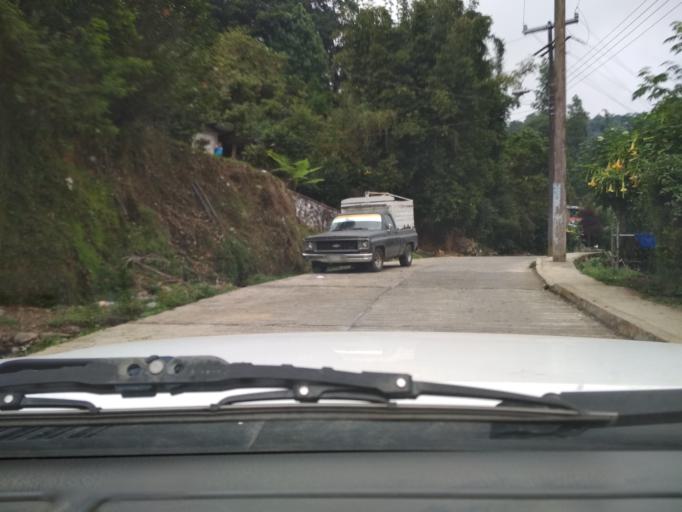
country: MX
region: Veracruz
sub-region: La Perla
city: Barrio de San Miguel
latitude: 18.9319
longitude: -97.1252
